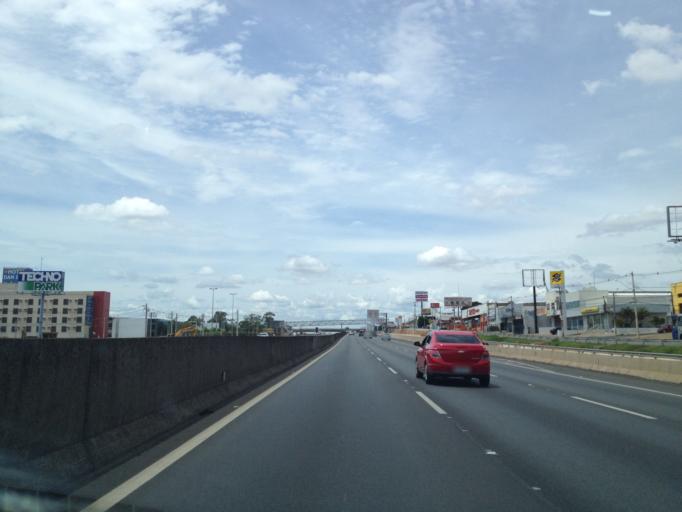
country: BR
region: Sao Paulo
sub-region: Hortolandia
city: Hortolandia
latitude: -22.8529
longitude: -47.1552
